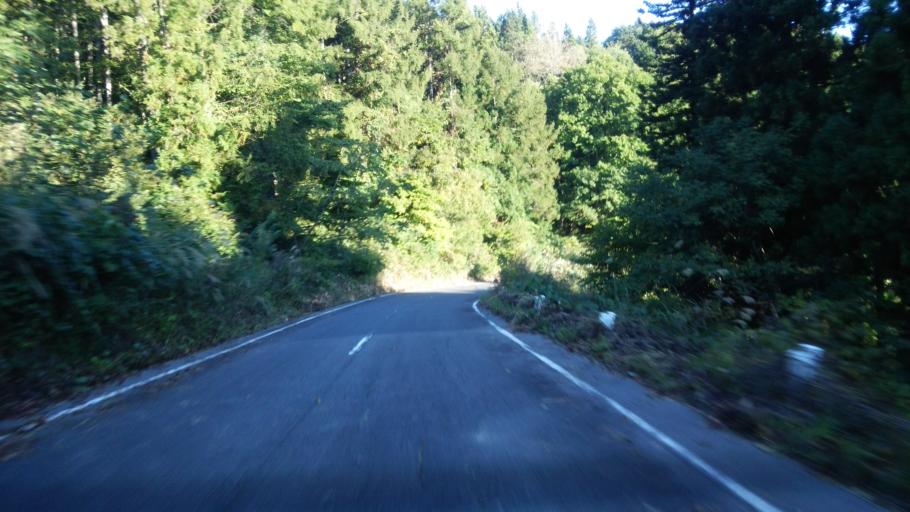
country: JP
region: Fukushima
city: Kitakata
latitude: 37.4073
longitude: 139.7649
